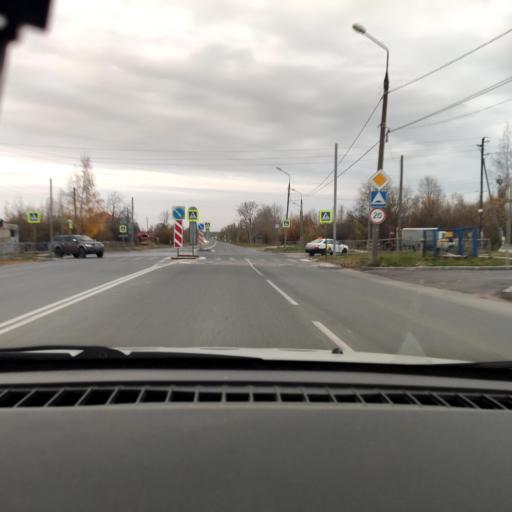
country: RU
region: Perm
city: Polazna
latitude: 58.1168
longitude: 56.4018
